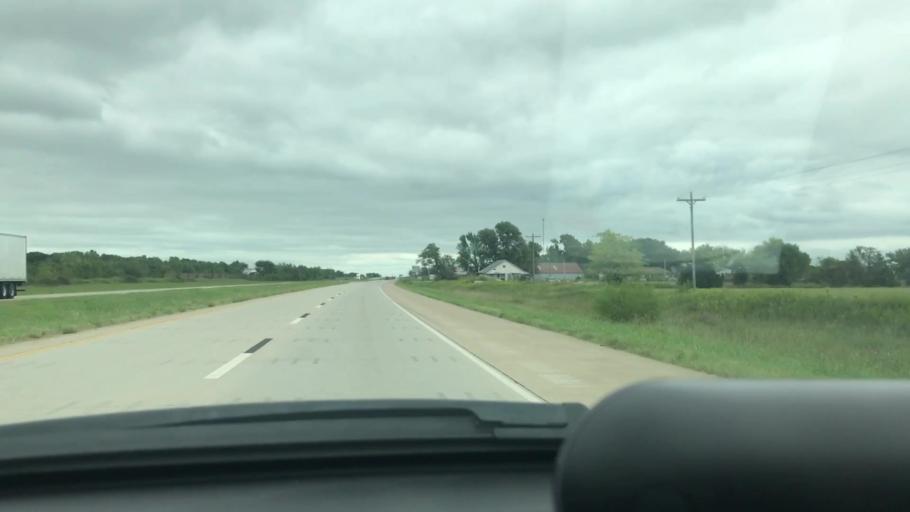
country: US
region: Oklahoma
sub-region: Mayes County
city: Chouteau
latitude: 36.0975
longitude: -95.3629
